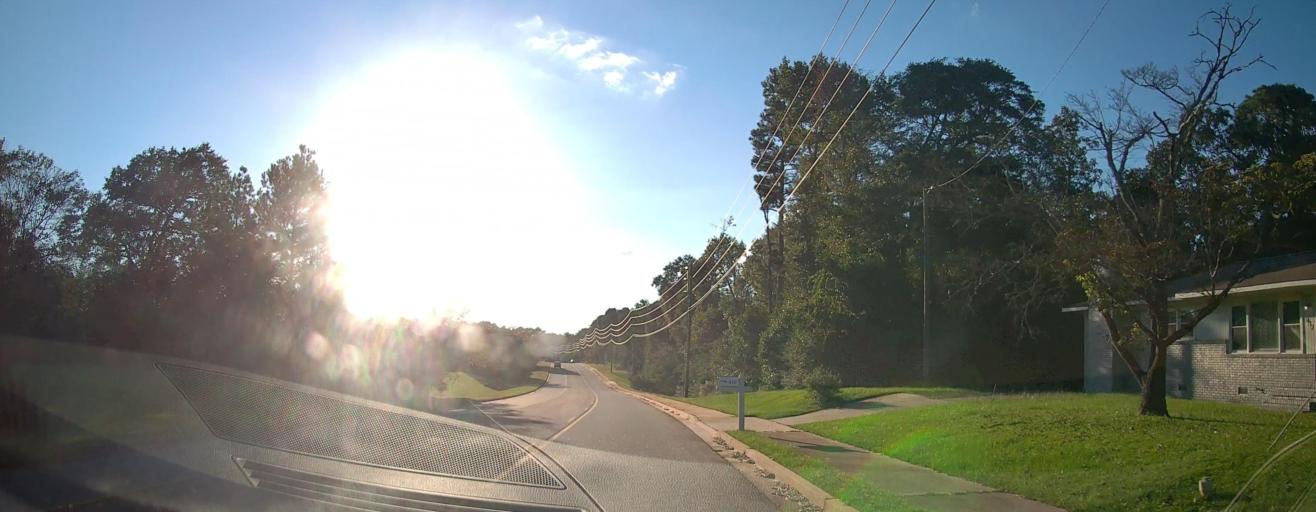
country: US
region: Georgia
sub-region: Houston County
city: Centerville
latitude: 32.6350
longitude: -83.6990
